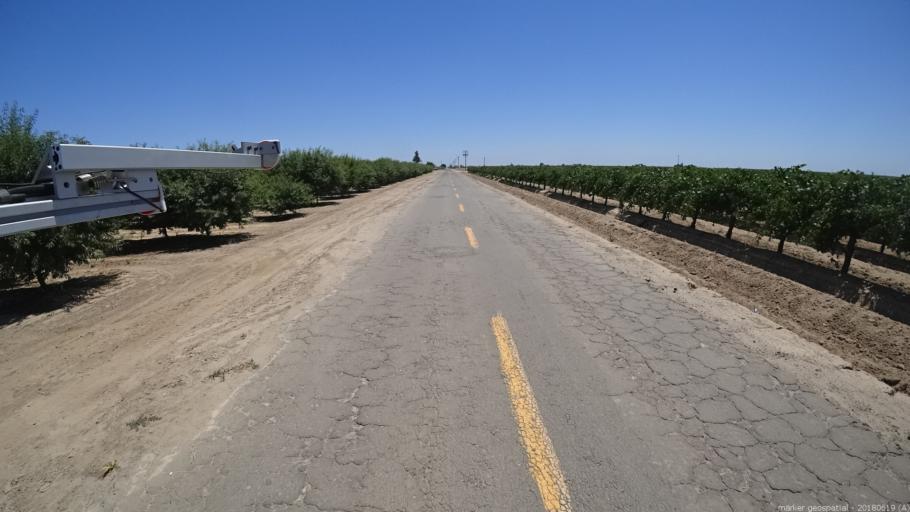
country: US
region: California
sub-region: Madera County
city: Parkwood
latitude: 36.8657
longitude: -120.1430
